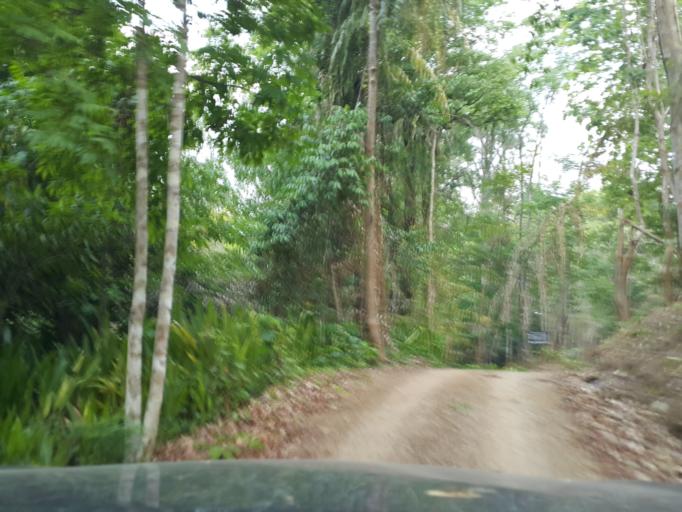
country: TH
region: Lamphun
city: Li
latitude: 17.6128
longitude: 98.9581
